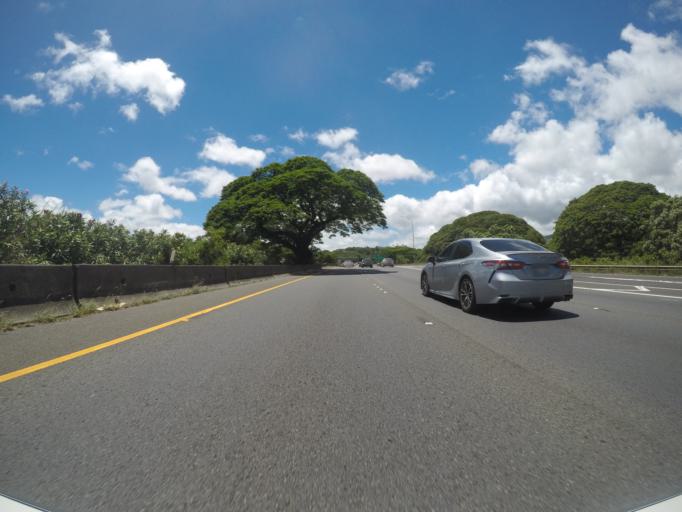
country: US
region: Hawaii
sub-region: Honolulu County
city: Halawa Heights
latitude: 21.3446
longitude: -157.8928
